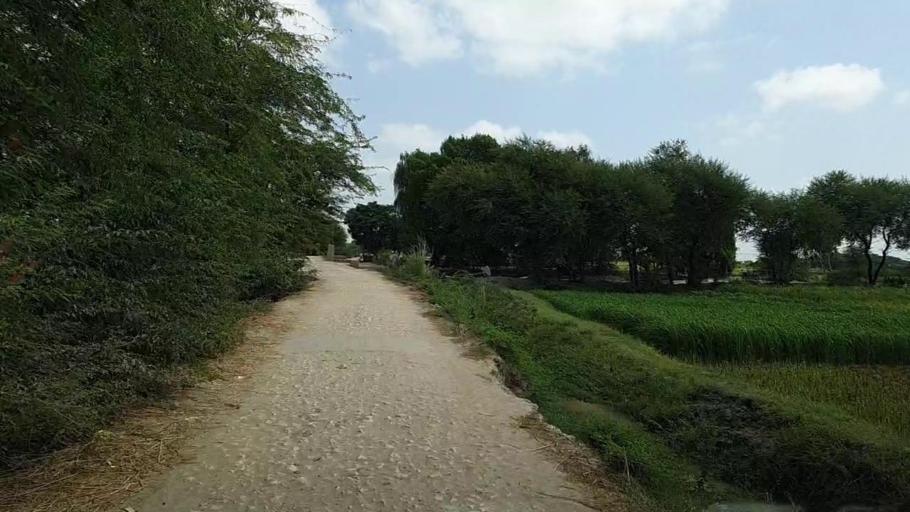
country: PK
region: Sindh
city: Kario
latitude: 24.6754
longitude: 68.5395
